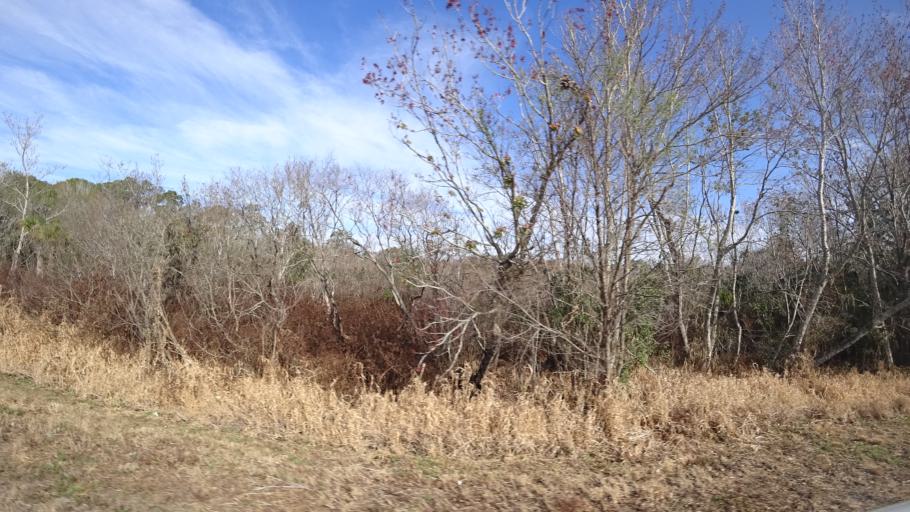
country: US
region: Florida
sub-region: Manatee County
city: Ellenton
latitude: 27.5941
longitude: -82.4457
